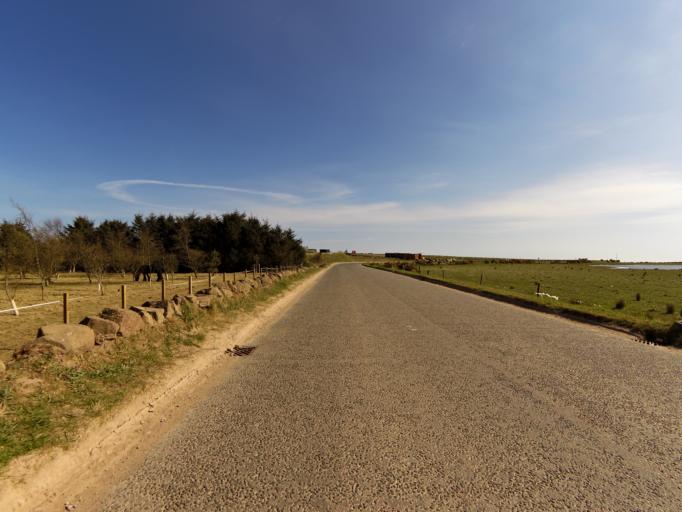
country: GB
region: Scotland
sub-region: Aberdeenshire
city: Portlethen
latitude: 57.0914
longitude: -2.0981
